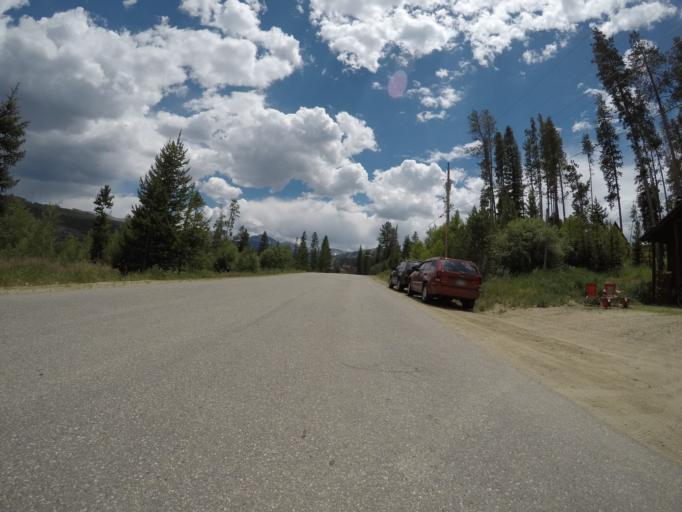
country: US
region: Colorado
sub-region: Grand County
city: Fraser
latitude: 39.9208
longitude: -105.7868
